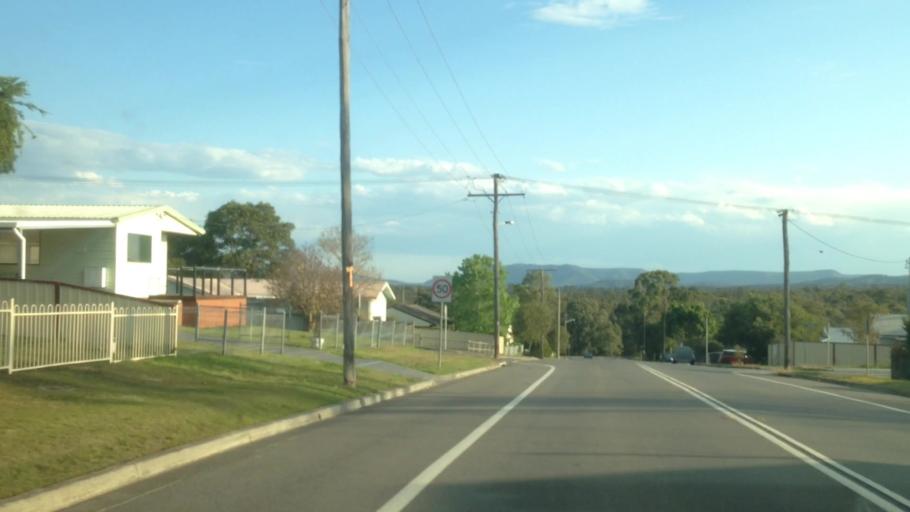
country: AU
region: New South Wales
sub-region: Cessnock
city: Kurri Kurri
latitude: -32.8315
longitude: 151.4809
